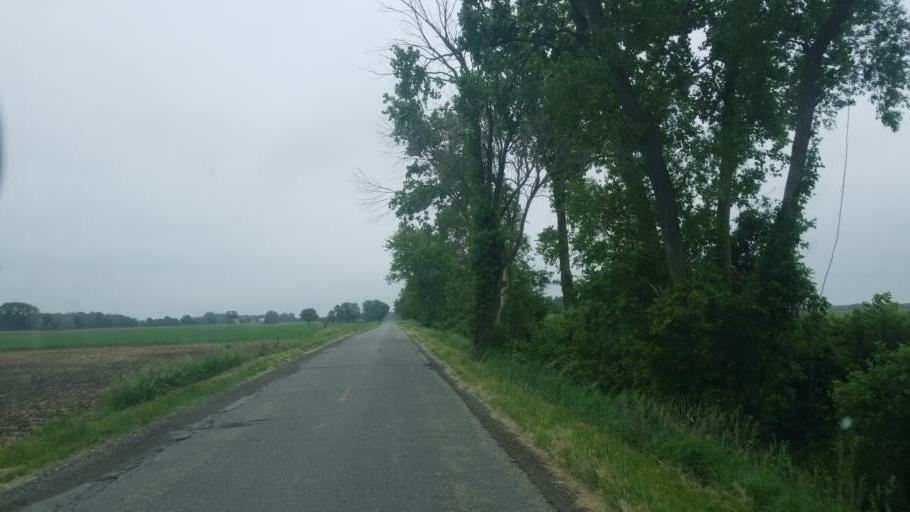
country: US
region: Indiana
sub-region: Marshall County
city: Bremen
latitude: 41.5003
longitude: -86.1179
